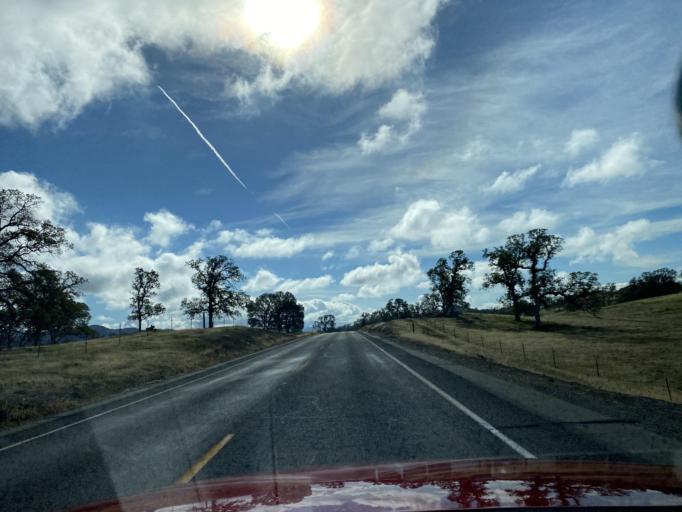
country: US
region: California
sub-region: Glenn County
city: Willows
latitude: 39.5175
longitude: -122.5288
